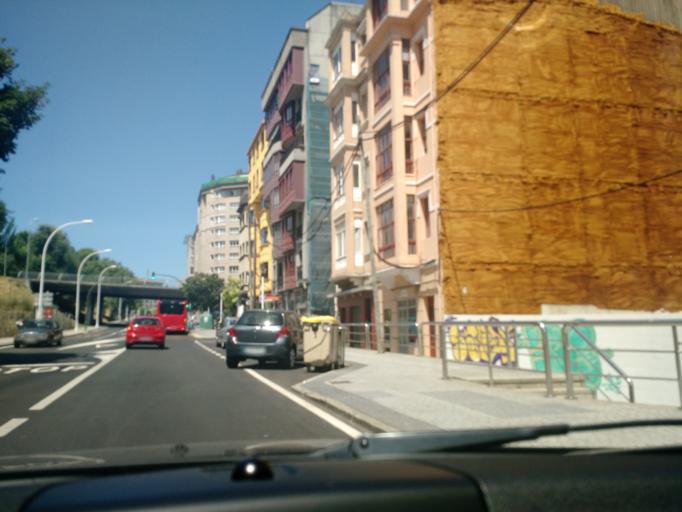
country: ES
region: Galicia
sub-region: Provincia da Coruna
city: A Coruna
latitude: 43.3507
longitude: -8.4048
